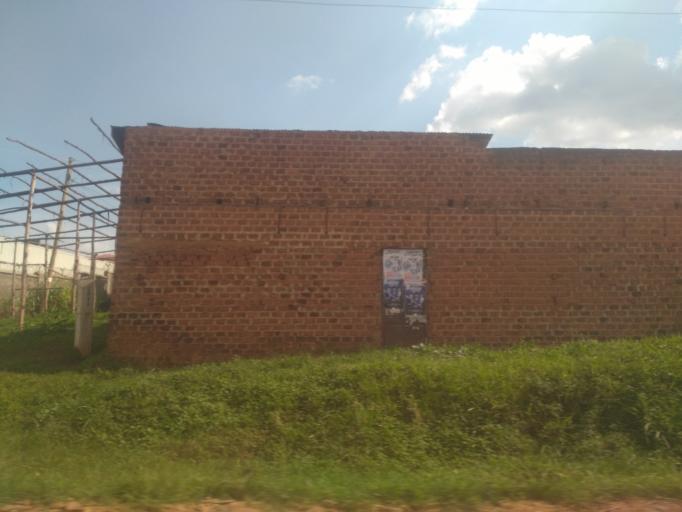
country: UG
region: Central Region
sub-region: Wakiso District
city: Kajansi
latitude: 0.2793
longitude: 32.4708
